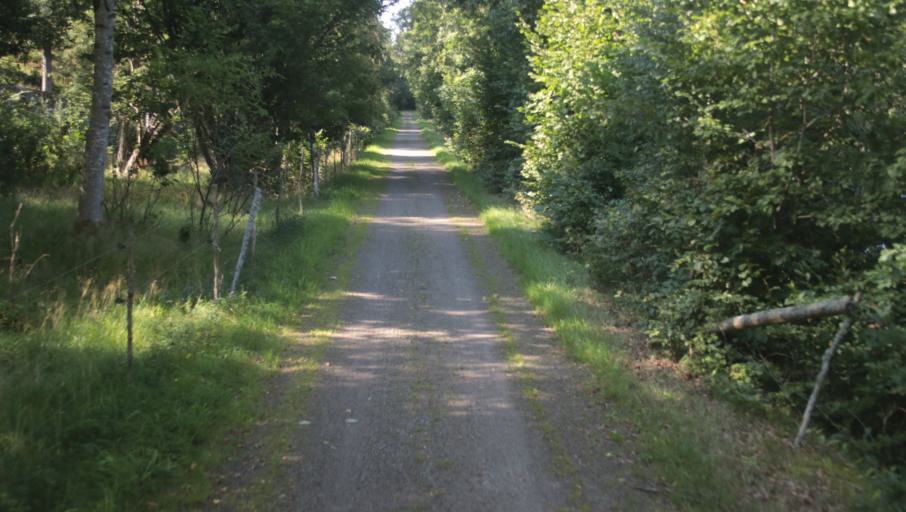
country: SE
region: Blekinge
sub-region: Karlshamns Kommun
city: Svangsta
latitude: 56.2795
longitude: 14.7564
